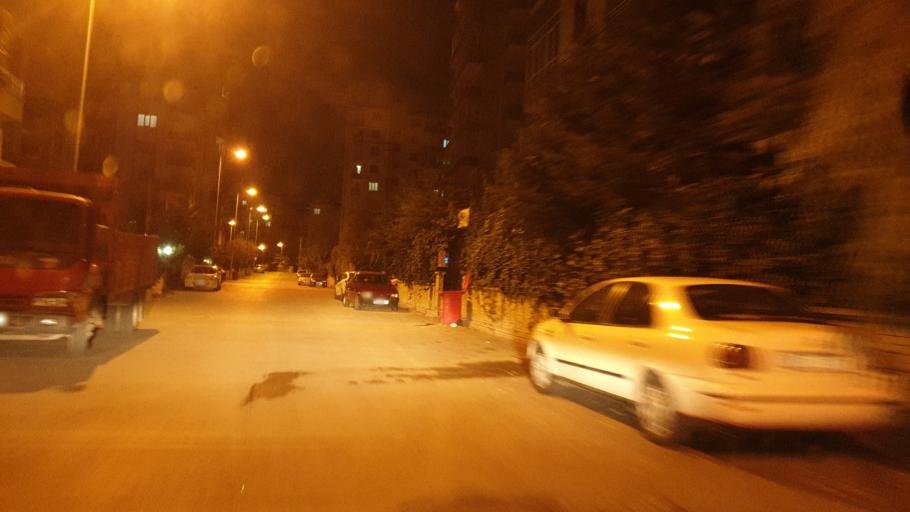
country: TR
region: Kayseri
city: Talas
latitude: 38.6962
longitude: 35.5418
